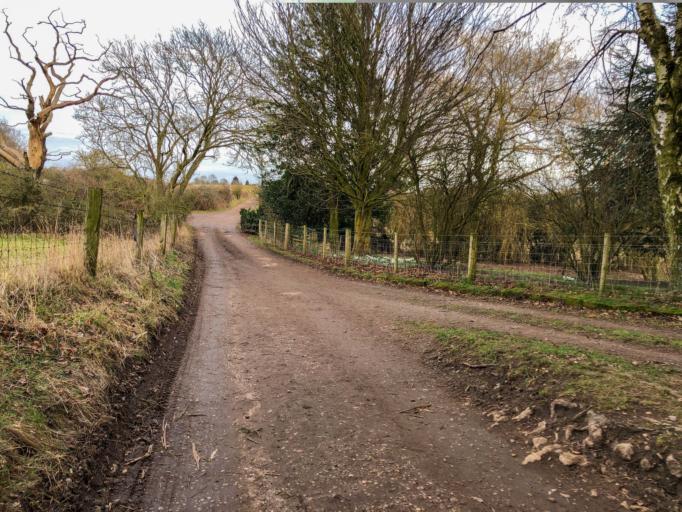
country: GB
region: England
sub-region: Warwickshire
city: Kenilworth
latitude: 52.3495
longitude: -1.6006
